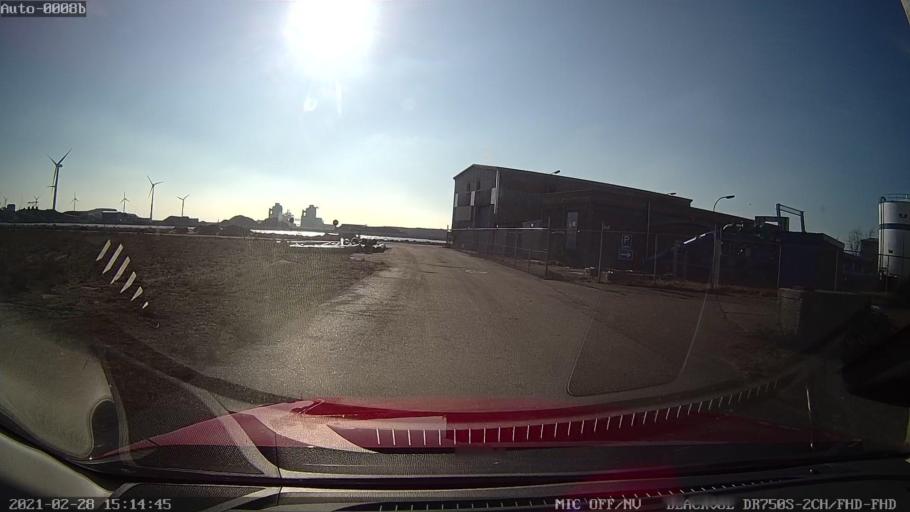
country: NL
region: Zeeland
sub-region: Gemeente Borsele
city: Borssele
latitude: 51.4563
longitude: 3.7020
